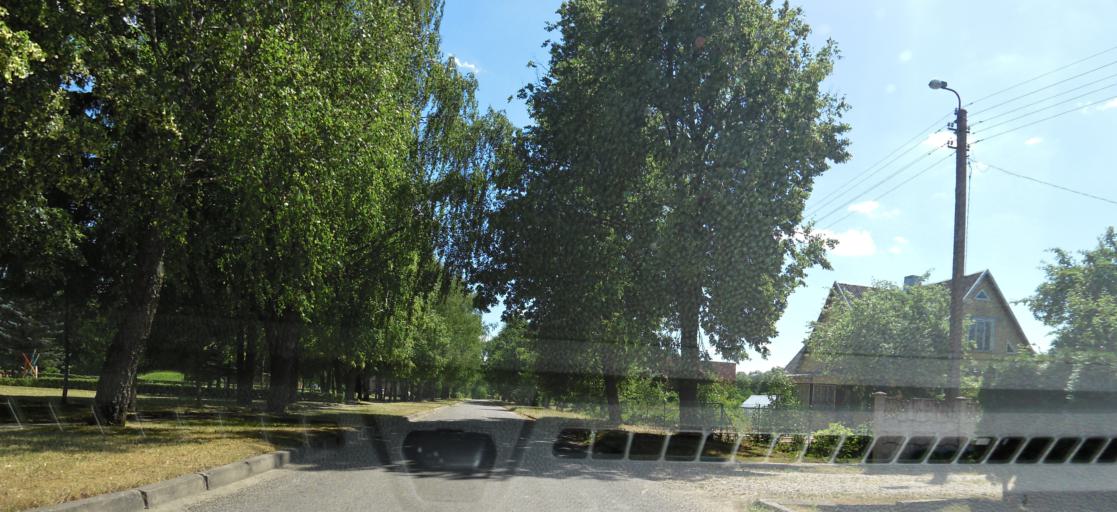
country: LT
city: Kupiskis
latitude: 55.9725
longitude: 24.9969
